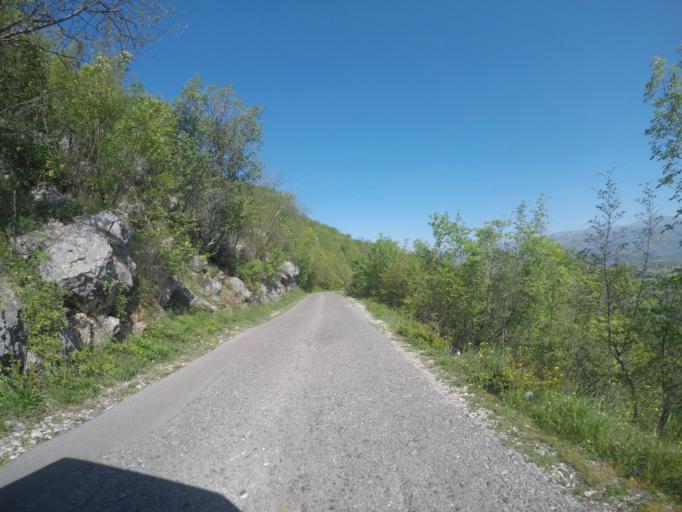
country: ME
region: Danilovgrad
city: Danilovgrad
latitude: 42.5203
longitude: 19.0955
